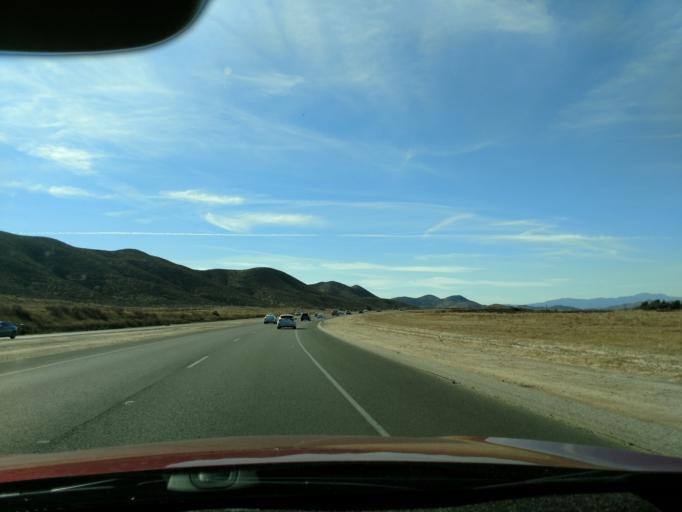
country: US
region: California
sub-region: Riverside County
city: Winchester
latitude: 33.7000
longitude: -117.0391
